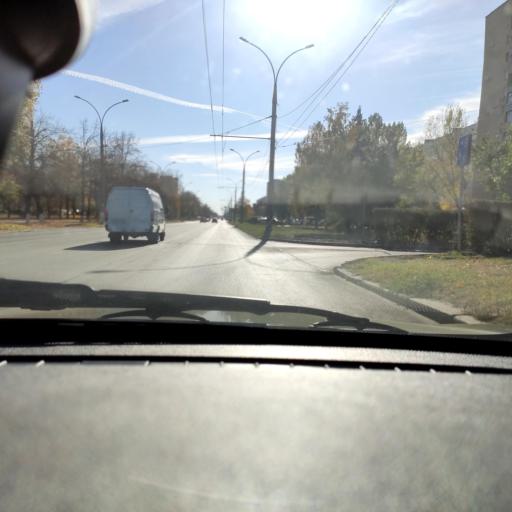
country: RU
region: Samara
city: Tol'yatti
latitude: 53.5332
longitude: 49.2773
